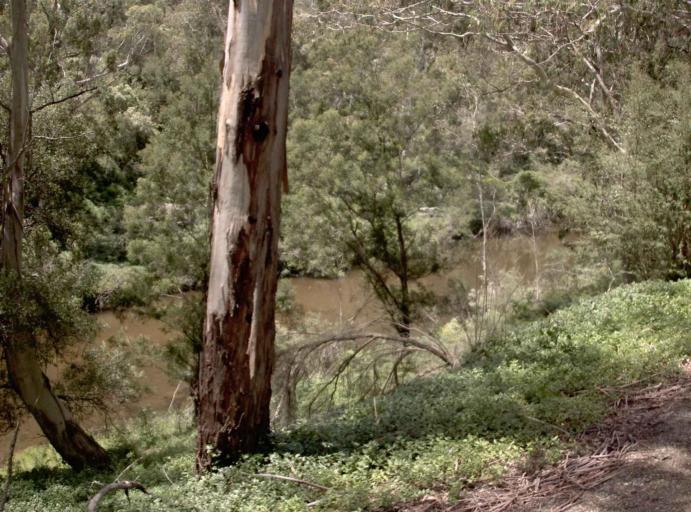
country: AU
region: Victoria
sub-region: East Gippsland
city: Lakes Entrance
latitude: -37.5388
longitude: 147.8645
